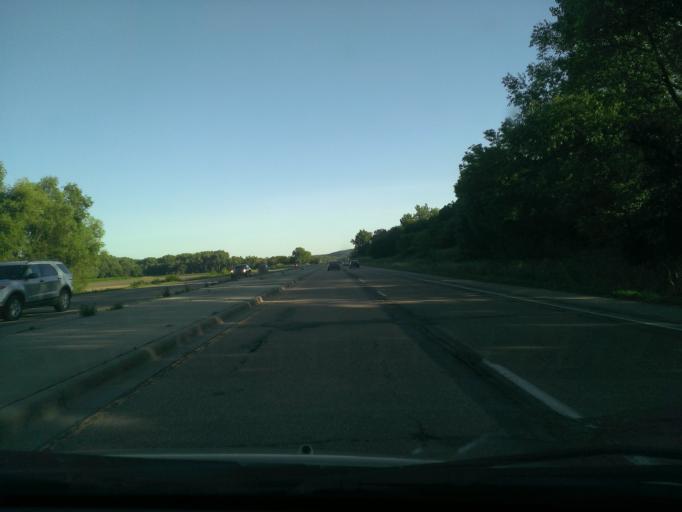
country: US
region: Minnesota
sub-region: Nicollet County
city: North Mankato
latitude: 44.2457
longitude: -94.0275
